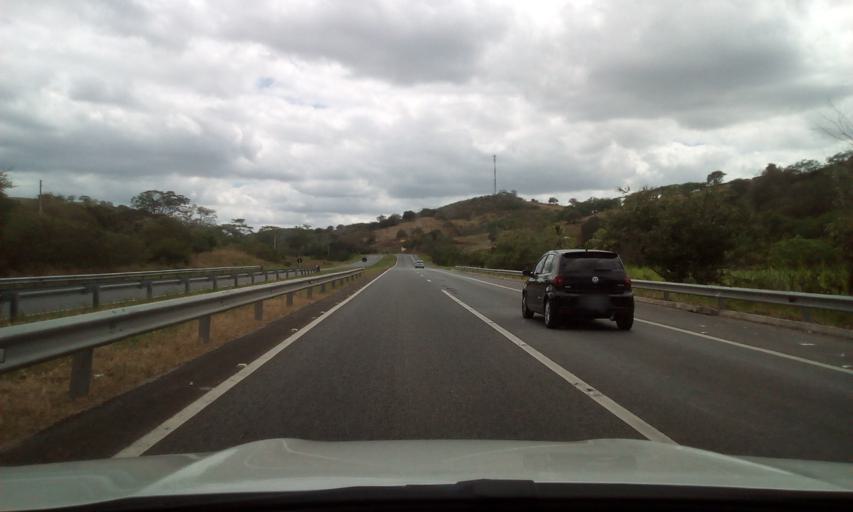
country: BR
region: Paraiba
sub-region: Fagundes
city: Fagundes
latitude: -7.2802
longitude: -35.7613
